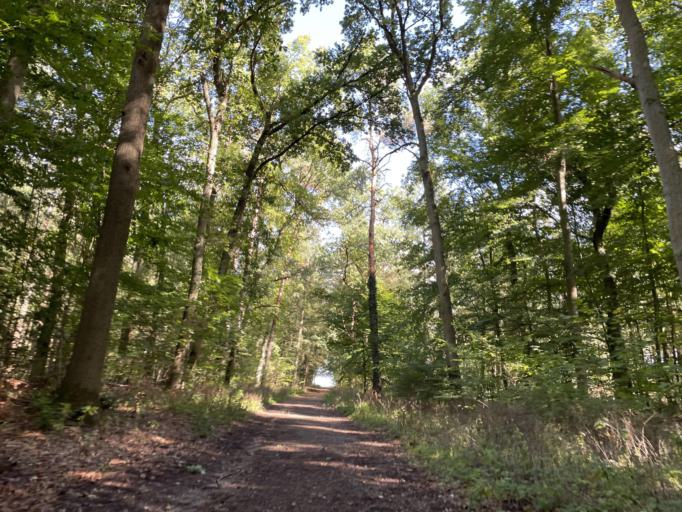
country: DE
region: Lower Saxony
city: Deutsch Evern
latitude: 53.2088
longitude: 10.4350
